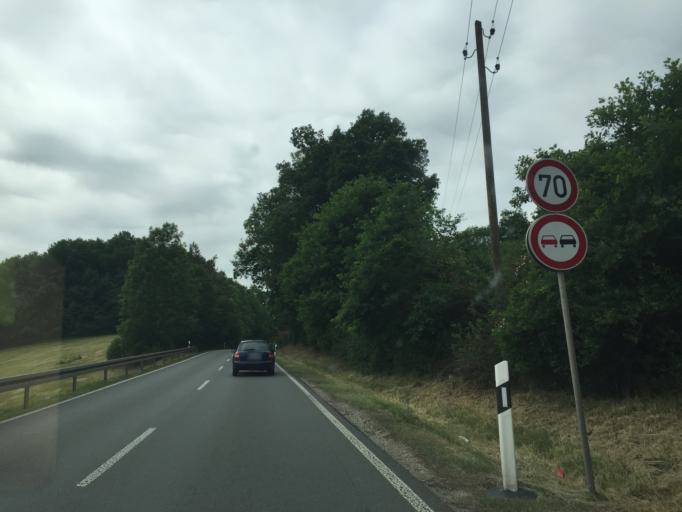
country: DE
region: Thuringia
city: Bad Blankenburg
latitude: 50.6941
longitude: 11.2295
